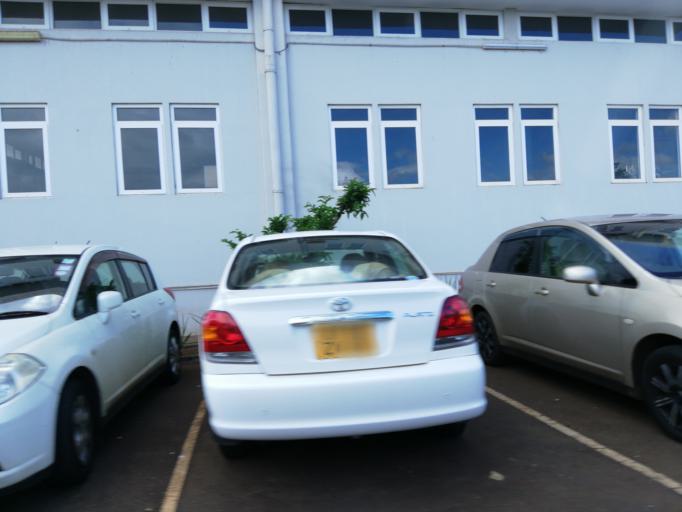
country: MU
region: Black River
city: Petite Riviere
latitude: -20.1887
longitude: 57.4643
